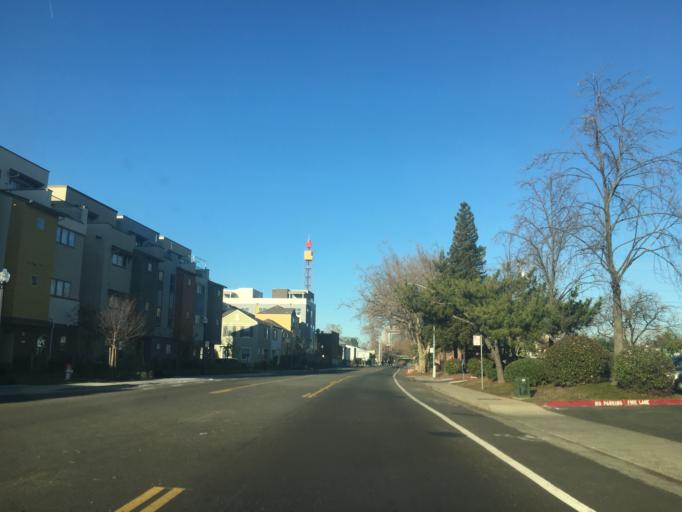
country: US
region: California
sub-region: Sacramento County
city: Sacramento
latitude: 38.5616
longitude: -121.5090
